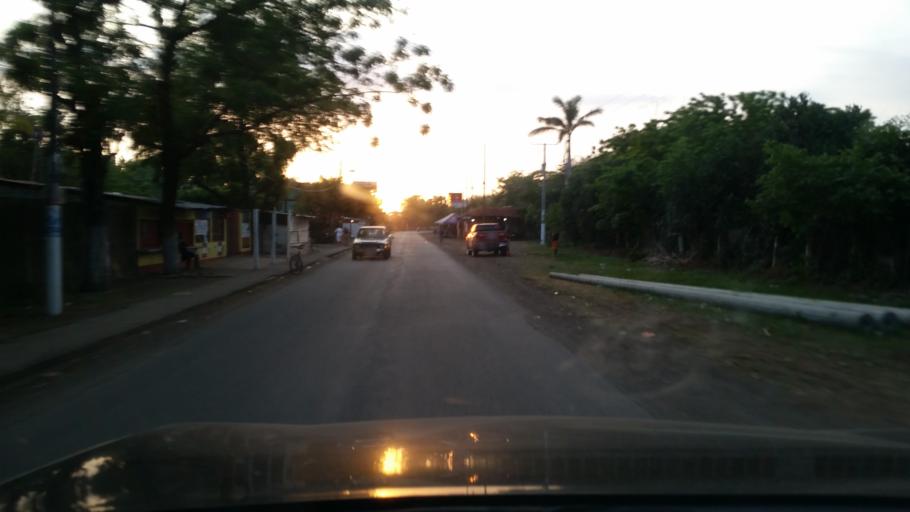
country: NI
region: Managua
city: Masachapa
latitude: 11.7791
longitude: -86.5127
